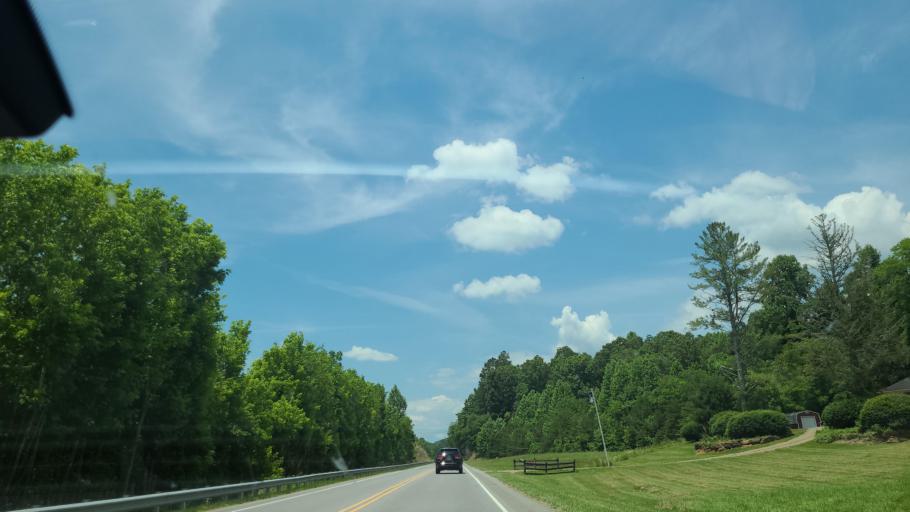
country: US
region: North Carolina
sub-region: Clay County
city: Hayesville
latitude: 35.0405
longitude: -83.8755
